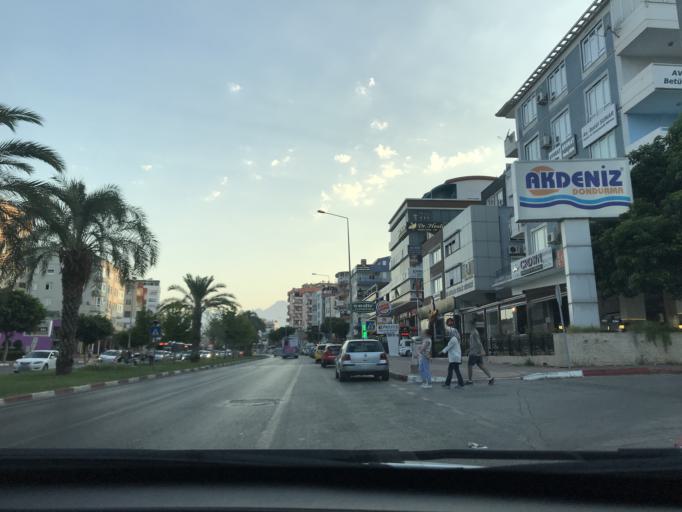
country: TR
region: Antalya
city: Antalya
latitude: 36.8768
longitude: 30.6451
